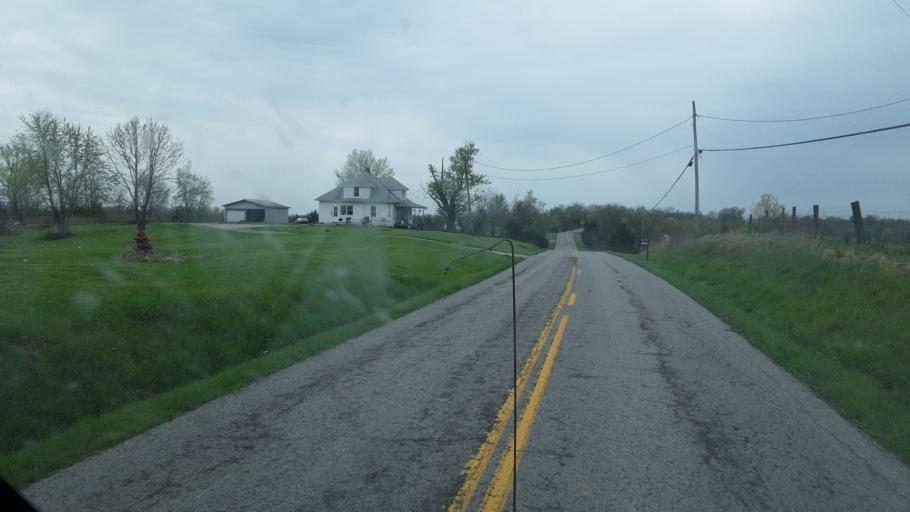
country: US
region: Kentucky
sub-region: Owen County
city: Owenton
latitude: 38.6436
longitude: -84.7524
